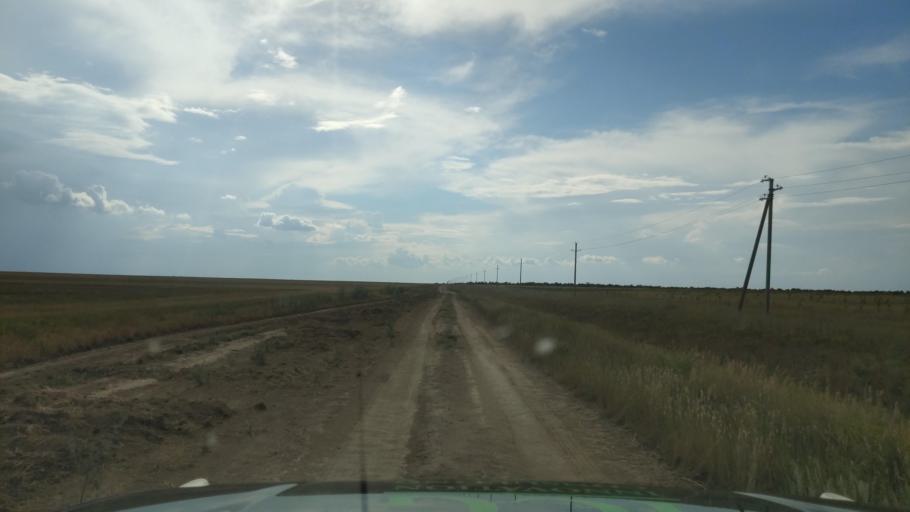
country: KZ
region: Pavlodar
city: Pavlodar
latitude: 52.5123
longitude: 77.5287
